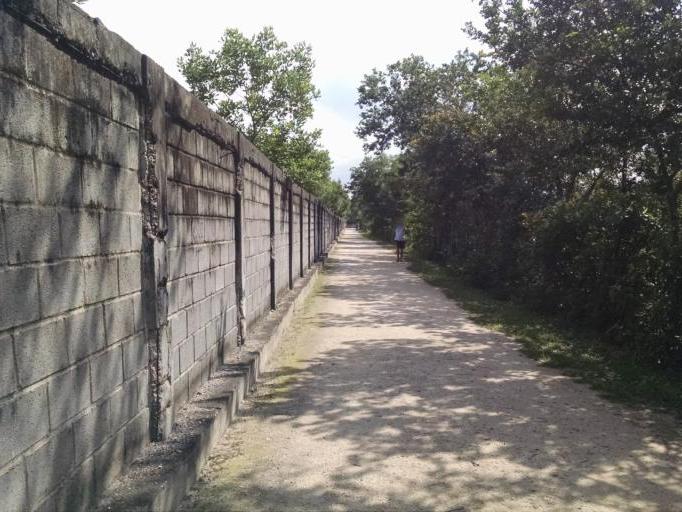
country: BR
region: Rio de Janeiro
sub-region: Rio De Janeiro
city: Rio de Janeiro
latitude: -22.9966
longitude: -43.3755
